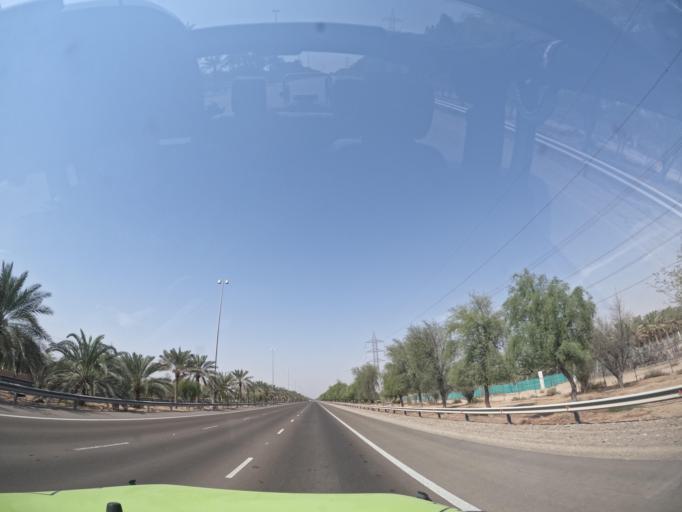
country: AE
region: Abu Dhabi
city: Al Ain
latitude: 24.2082
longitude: 55.4406
